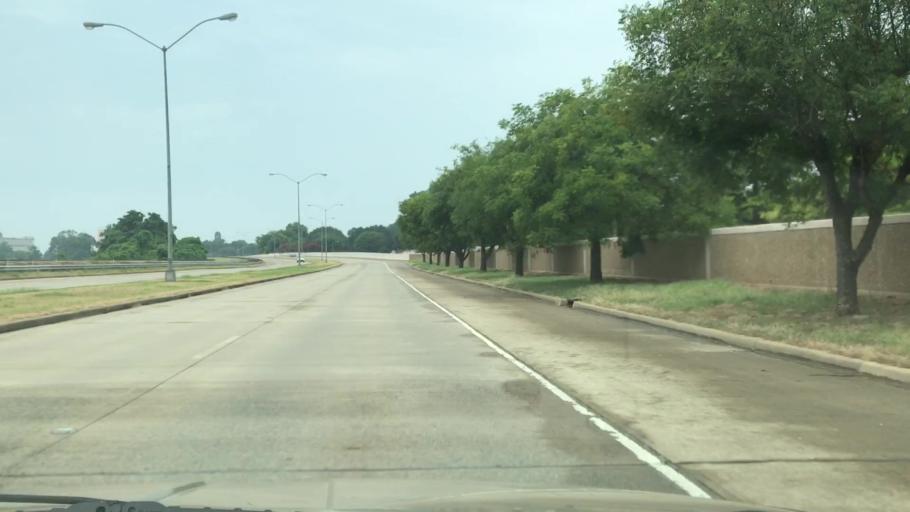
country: US
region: Louisiana
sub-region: Bossier Parish
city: Bossier City
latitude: 32.5081
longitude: -93.7145
